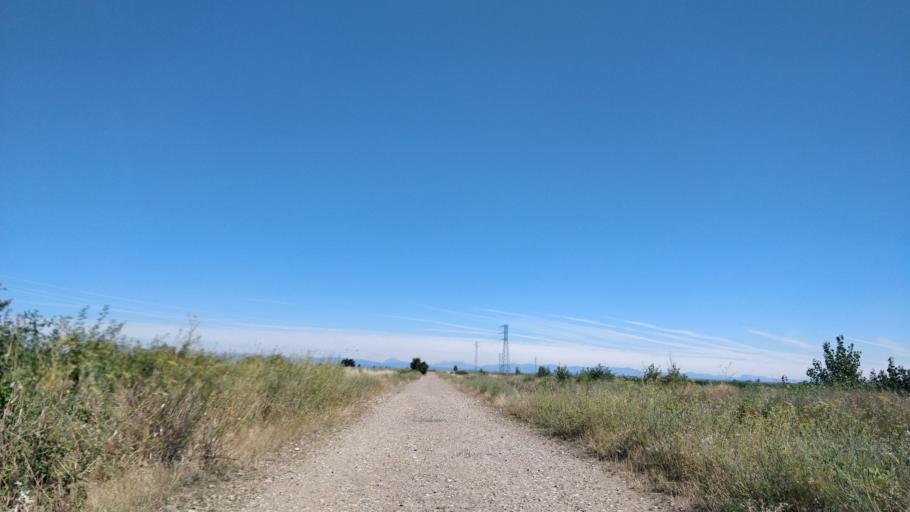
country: ES
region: Castille and Leon
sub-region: Provincia de Leon
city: Bustillo del Paramo
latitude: 42.4271
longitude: -5.8215
